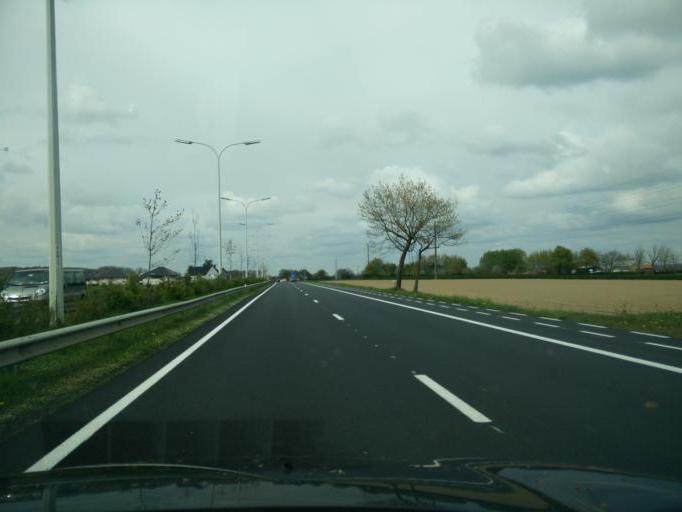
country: BE
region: Flanders
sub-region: Provincie Oost-Vlaanderen
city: Oudenaarde
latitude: 50.8861
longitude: 3.6161
